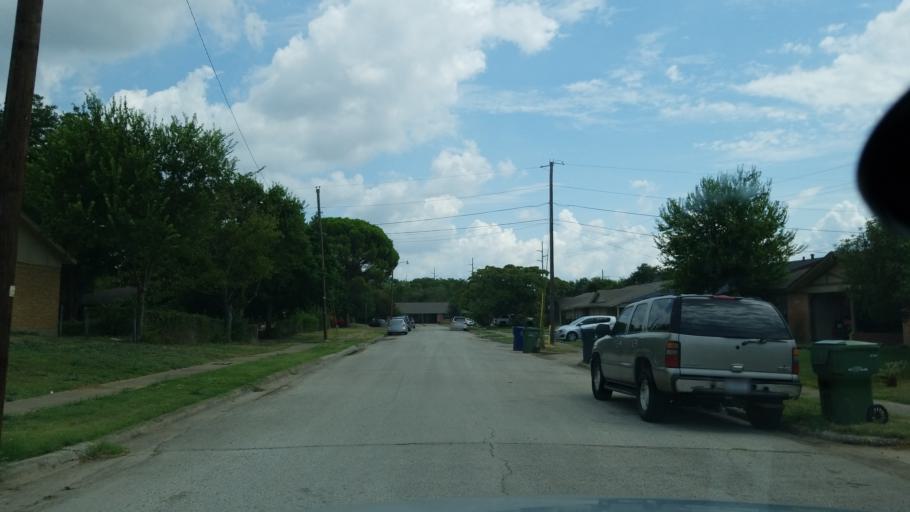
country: US
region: Texas
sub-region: Dallas County
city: Garland
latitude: 32.9139
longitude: -96.6547
